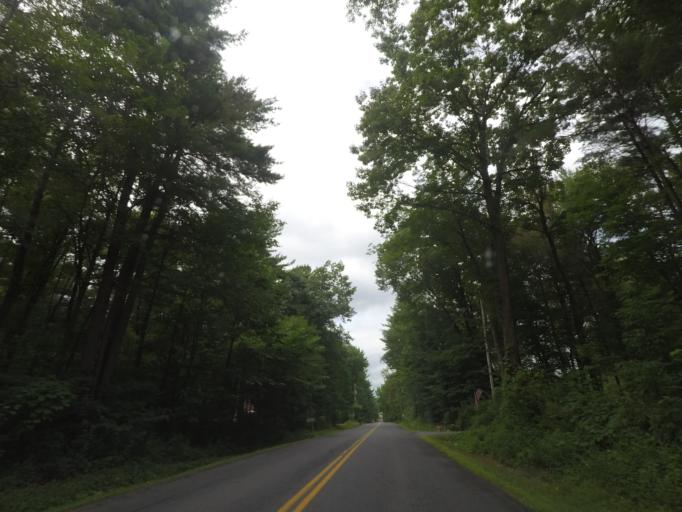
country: US
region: New York
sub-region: Saratoga County
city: Stillwater
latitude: 42.9957
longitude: -73.6924
